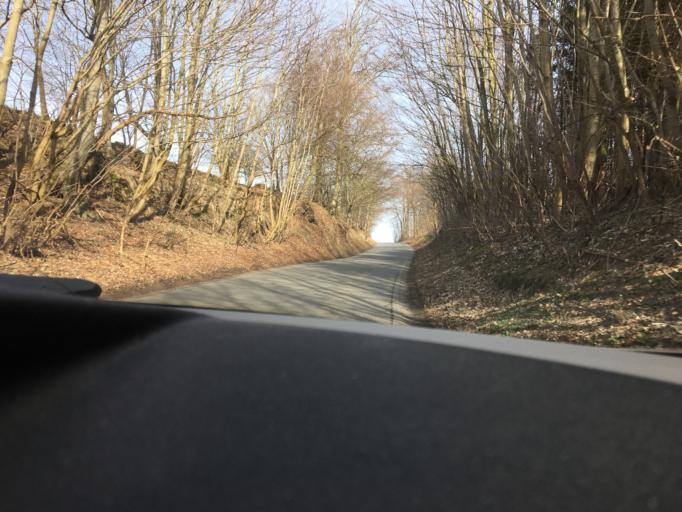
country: DK
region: South Denmark
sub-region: Vejle Kommune
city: Brejning
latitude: 55.7223
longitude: 9.6360
